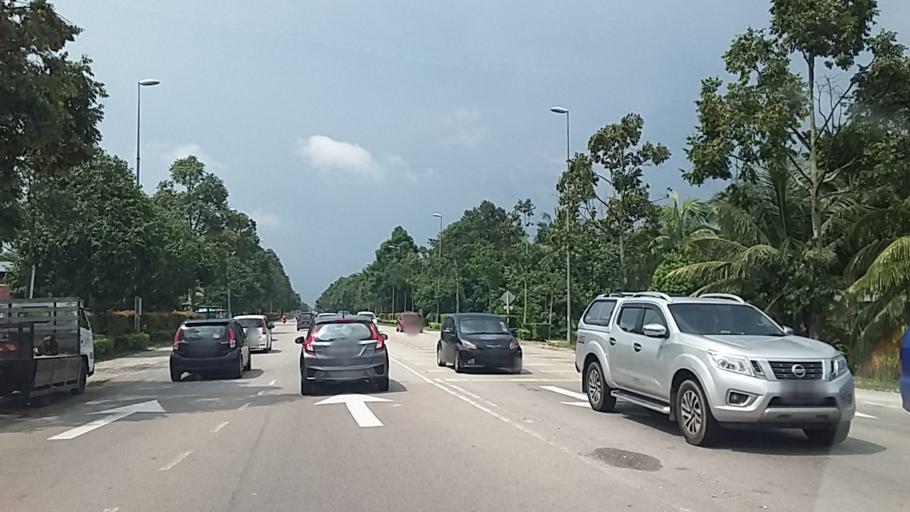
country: MY
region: Johor
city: Parit Raja
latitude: 1.8578
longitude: 103.1001
